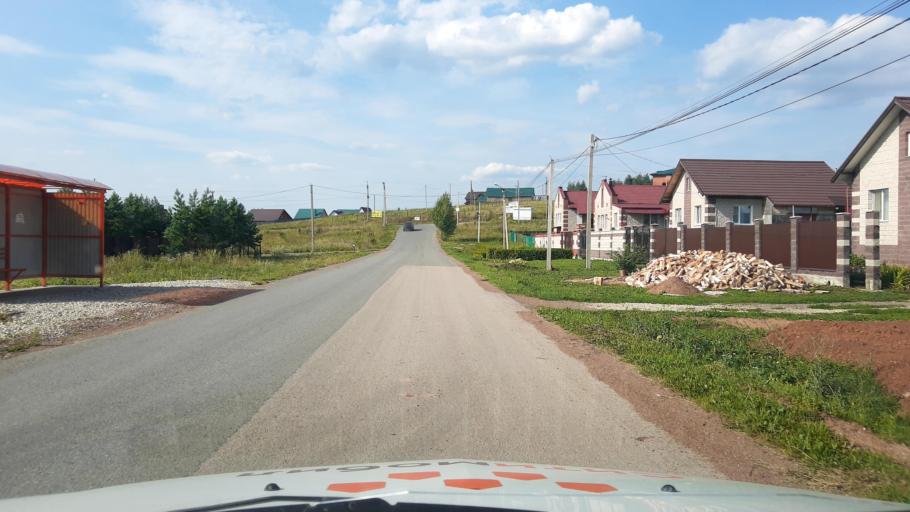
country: RU
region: Bashkortostan
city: Kabakovo
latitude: 54.6654
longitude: 56.2139
